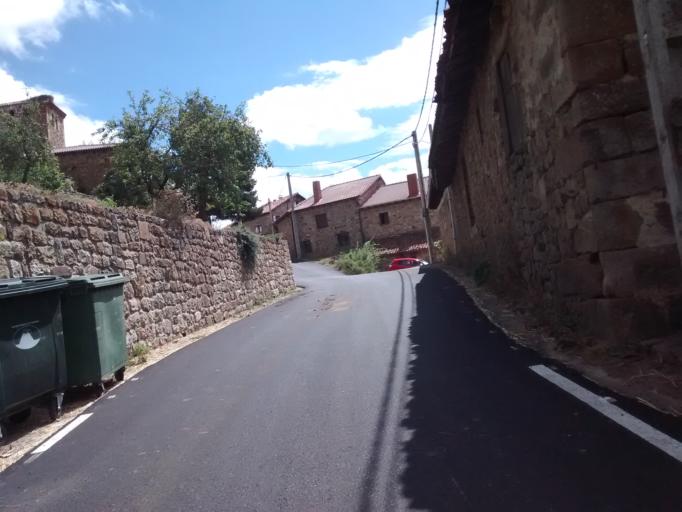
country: ES
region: Castille and Leon
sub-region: Provincia de Palencia
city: San Cebrian de Muda
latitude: 42.9452
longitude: -4.4328
